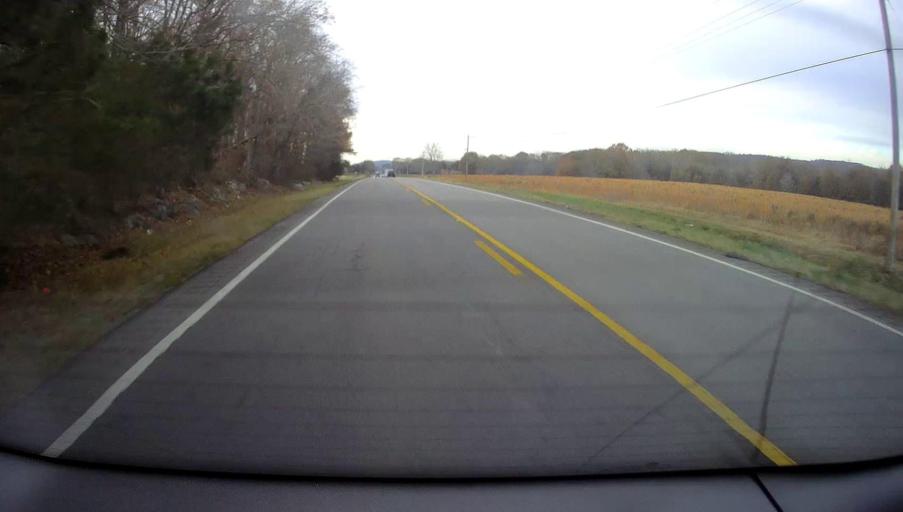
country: US
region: Alabama
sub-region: Marshall County
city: Arab
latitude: 34.3986
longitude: -86.6806
